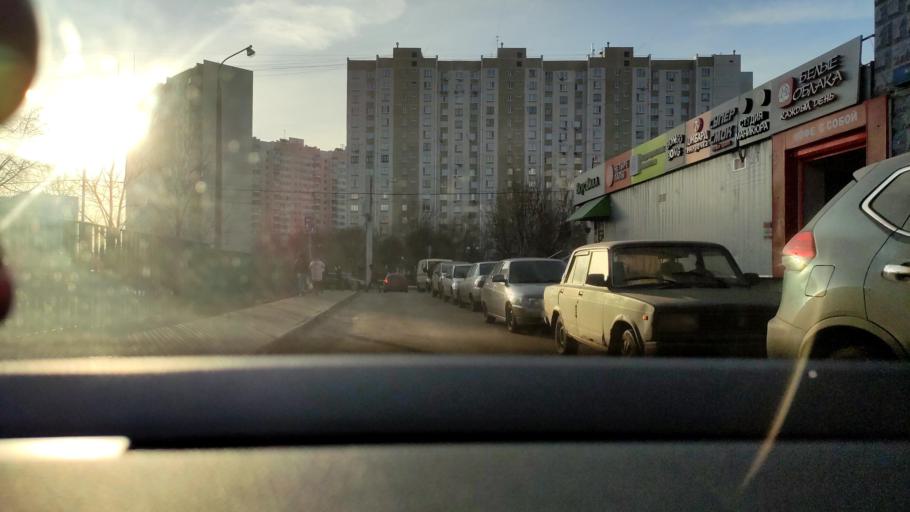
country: RU
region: Moskovskaya
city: Pavshino
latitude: 55.8460
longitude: 37.3639
